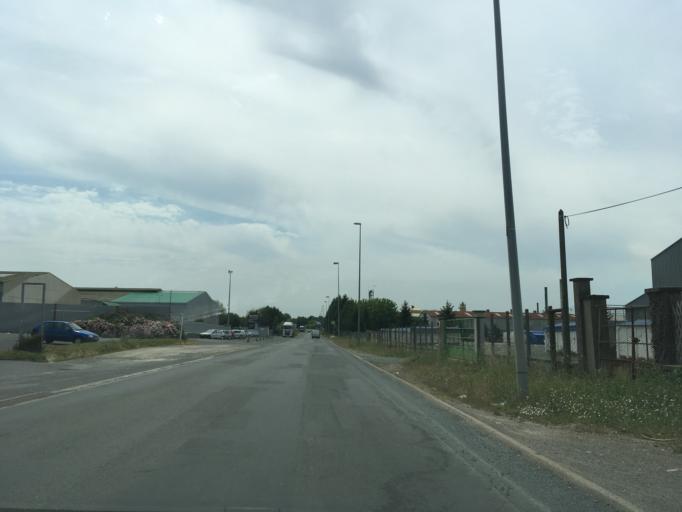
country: FR
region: Poitou-Charentes
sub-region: Departement des Deux-Sevres
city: Niort
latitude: 46.3044
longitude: -0.4601
